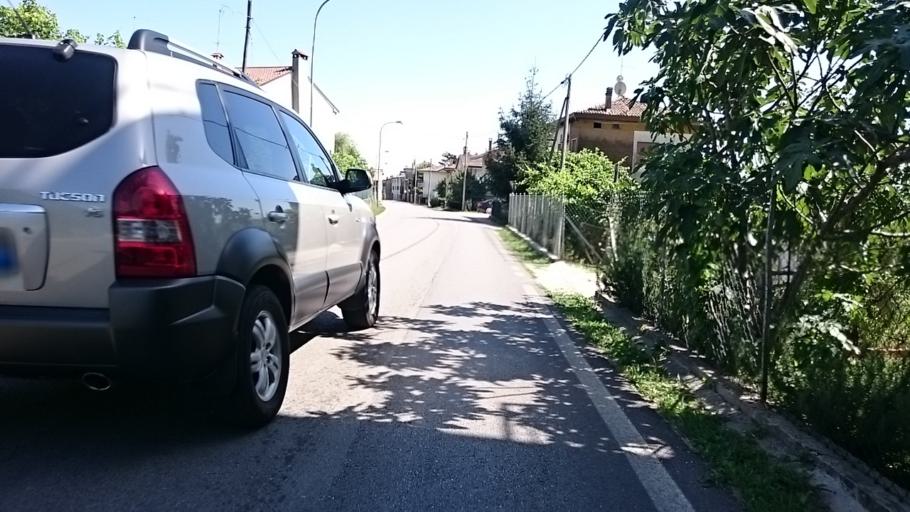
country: IT
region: Veneto
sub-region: Provincia di Treviso
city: Col San Martino
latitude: 45.9017
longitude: 12.0809
